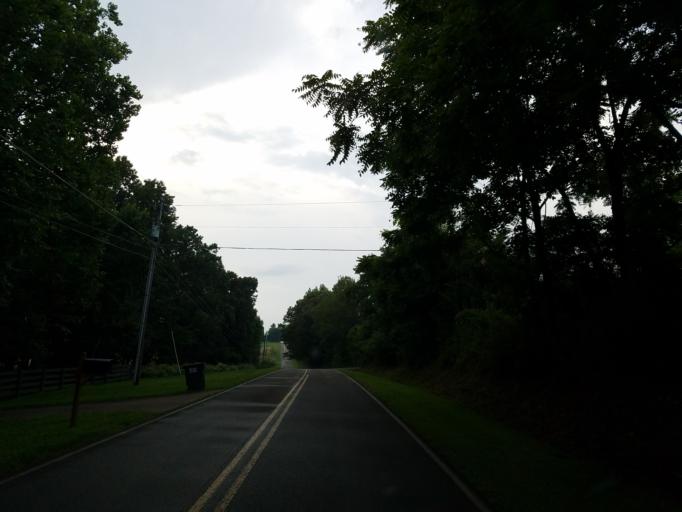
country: US
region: Georgia
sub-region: Pickens County
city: Jasper
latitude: 34.4909
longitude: -84.5147
